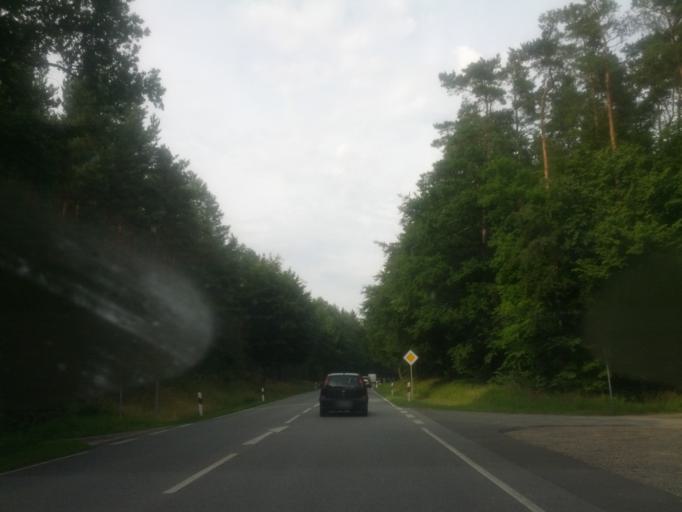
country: DE
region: Mecklenburg-Vorpommern
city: Neubukow
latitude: 54.0063
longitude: 11.6428
